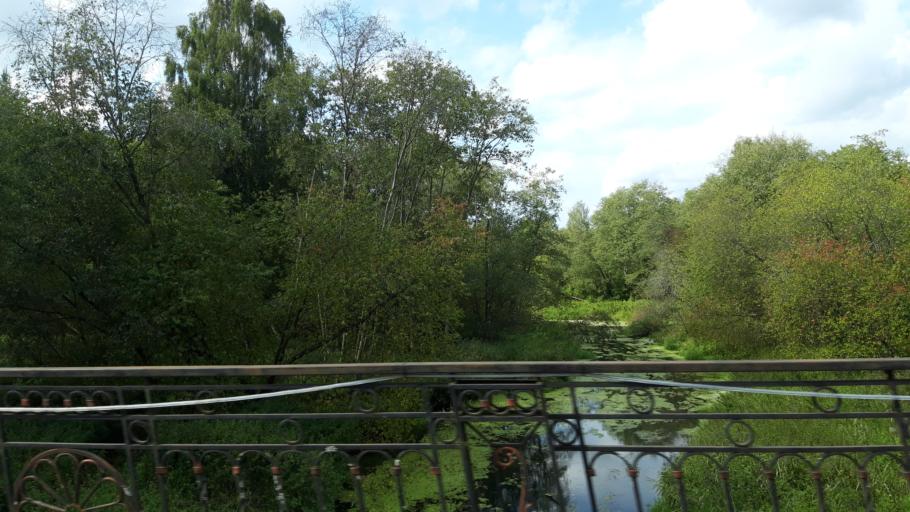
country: RU
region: Moskovskaya
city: Mendeleyevo
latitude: 56.0470
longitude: 37.2165
